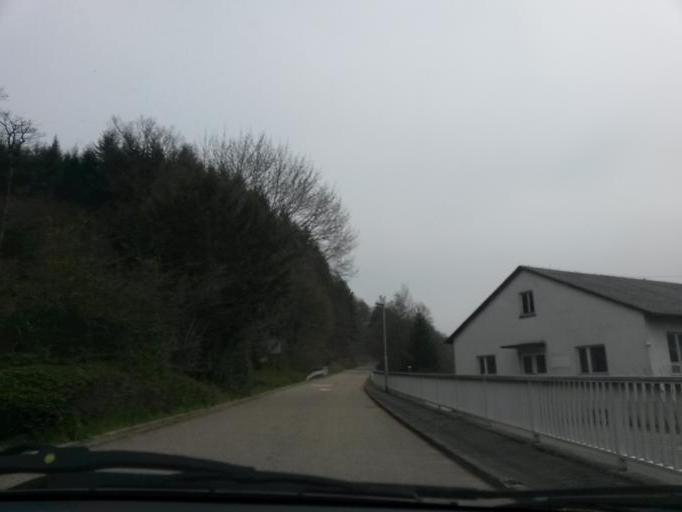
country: DE
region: Baden-Wuerttemberg
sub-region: Freiburg Region
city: Lahr
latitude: 48.3102
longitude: 7.8633
